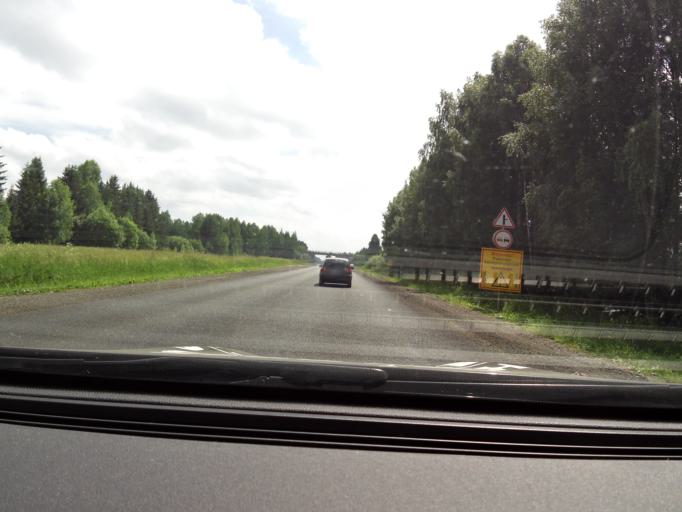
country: RU
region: Perm
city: Bershet'
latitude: 57.7116
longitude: 56.3701
